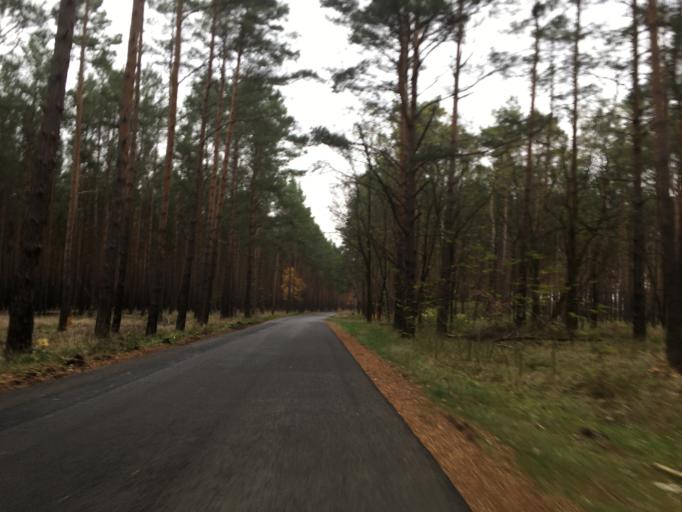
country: DE
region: Brandenburg
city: Mullrose
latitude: 52.2645
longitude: 14.4775
